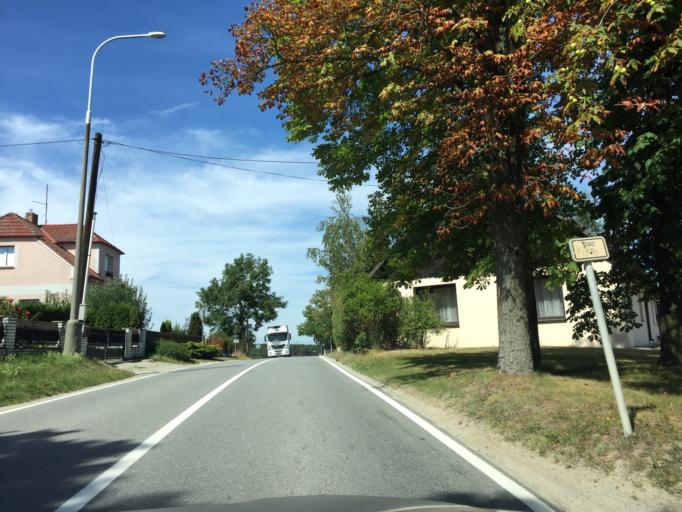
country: CZ
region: Jihocesky
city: Sevetin
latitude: 49.1021
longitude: 14.5728
